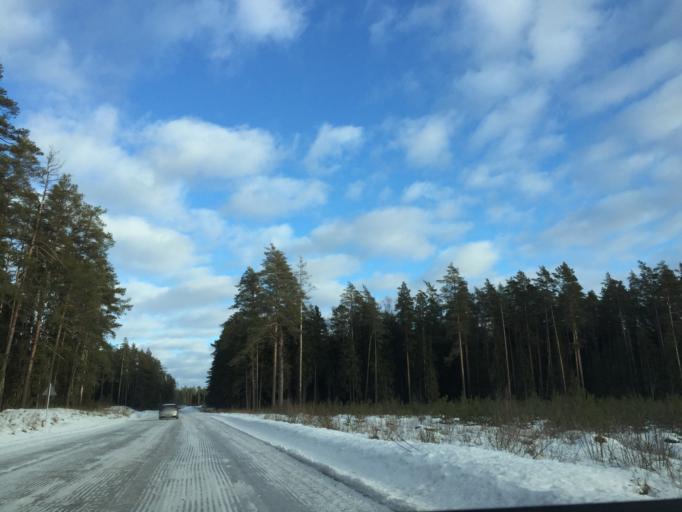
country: LV
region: Ogre
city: Jumprava
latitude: 56.5871
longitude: 24.9679
